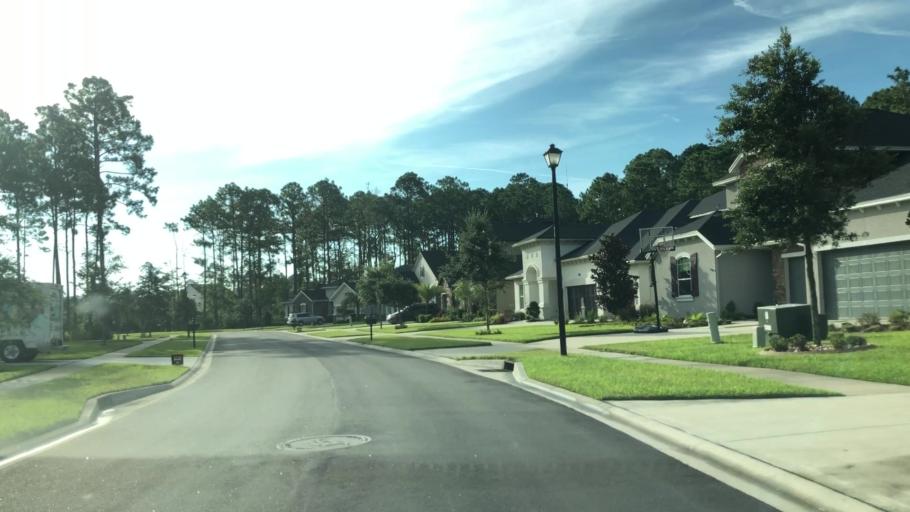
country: US
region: Florida
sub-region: Saint Johns County
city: Palm Valley
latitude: 30.1309
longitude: -81.4268
